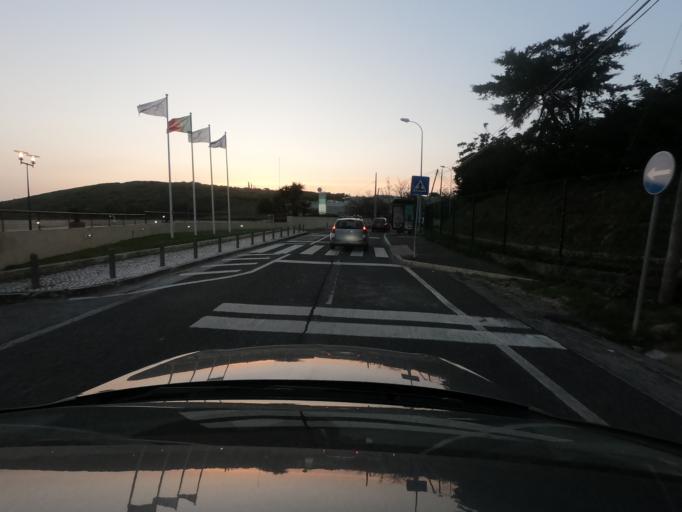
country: PT
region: Lisbon
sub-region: Amadora
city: Amadora
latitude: 38.7358
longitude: -9.2305
